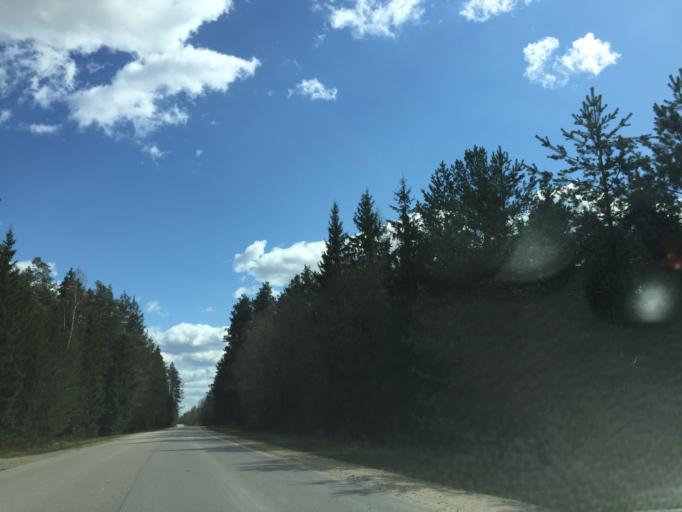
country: LV
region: Vilanu
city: Vilani
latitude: 56.5707
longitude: 27.0475
